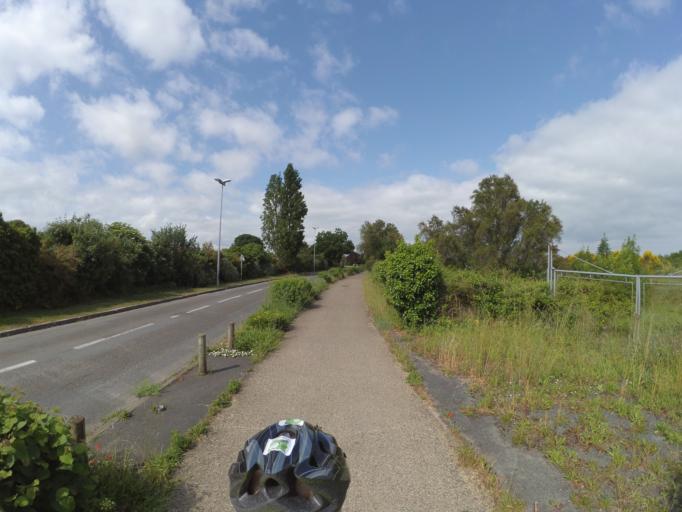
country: FR
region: Poitou-Charentes
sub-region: Departement de la Charente-Maritime
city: Angoulins
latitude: 46.1059
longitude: -1.1170
